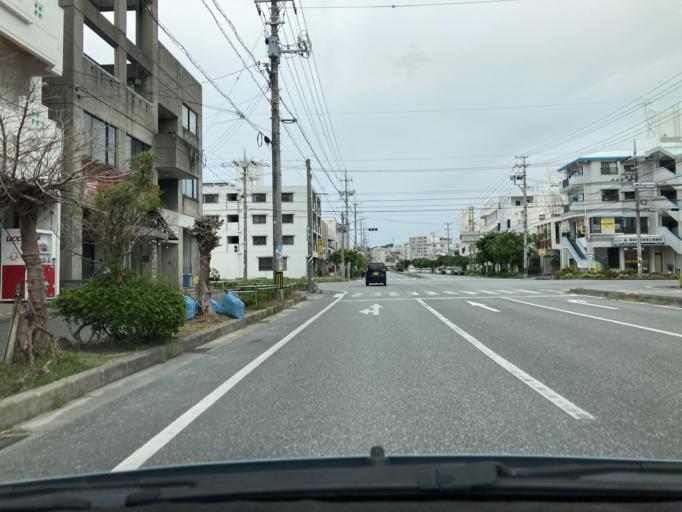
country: JP
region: Okinawa
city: Itoman
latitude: 26.1405
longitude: 127.6657
